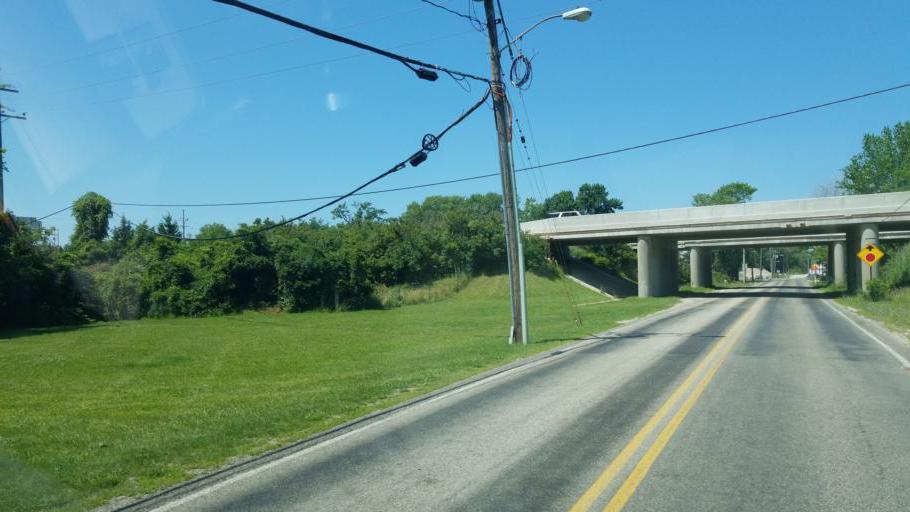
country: US
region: Ohio
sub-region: Ottawa County
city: Port Clinton
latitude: 41.5065
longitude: -82.8707
